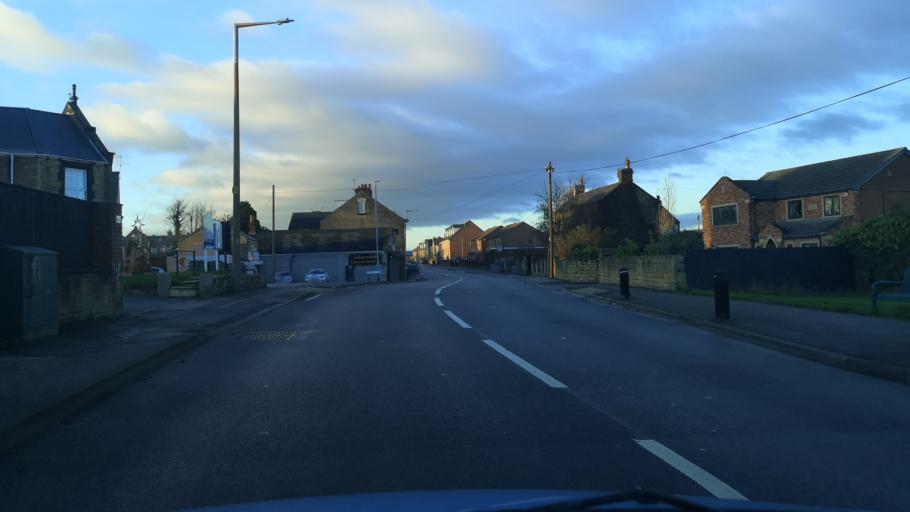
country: GB
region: England
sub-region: Barnsley
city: Great Houghton
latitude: 53.5540
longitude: -1.3511
